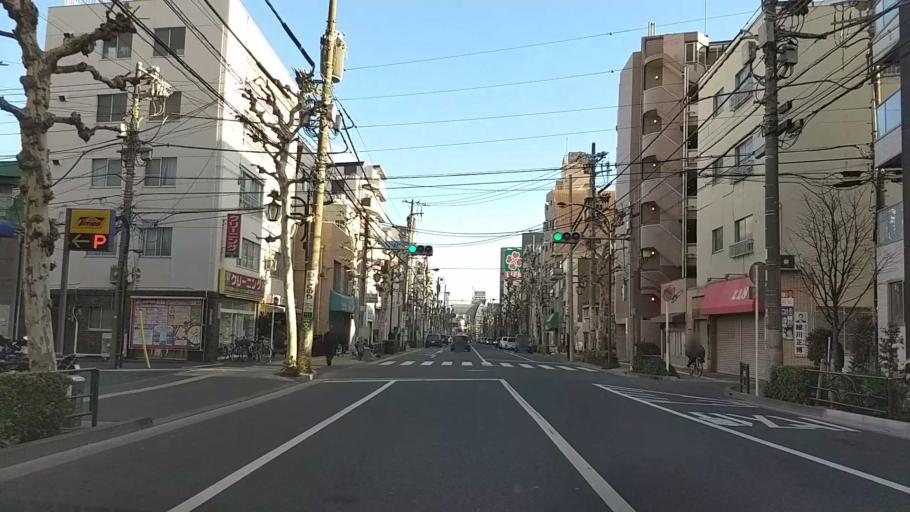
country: JP
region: Tokyo
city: Tokyo
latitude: 35.7281
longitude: 139.7326
